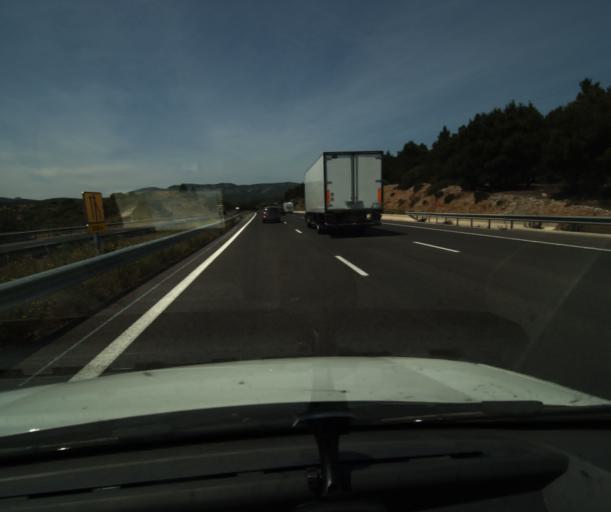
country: FR
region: Languedoc-Roussillon
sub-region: Departement de l'Aude
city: Leucate
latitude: 42.9219
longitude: 2.9780
